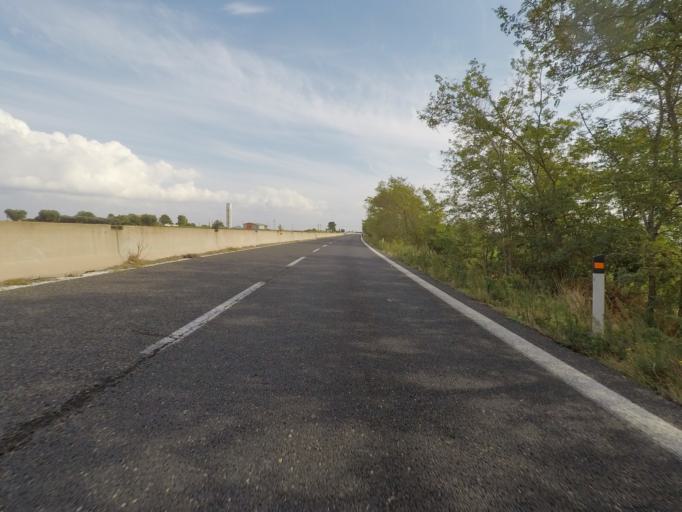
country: IT
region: Latium
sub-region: Provincia di Viterbo
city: Montalto di Castro
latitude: 42.3658
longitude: 11.5762
